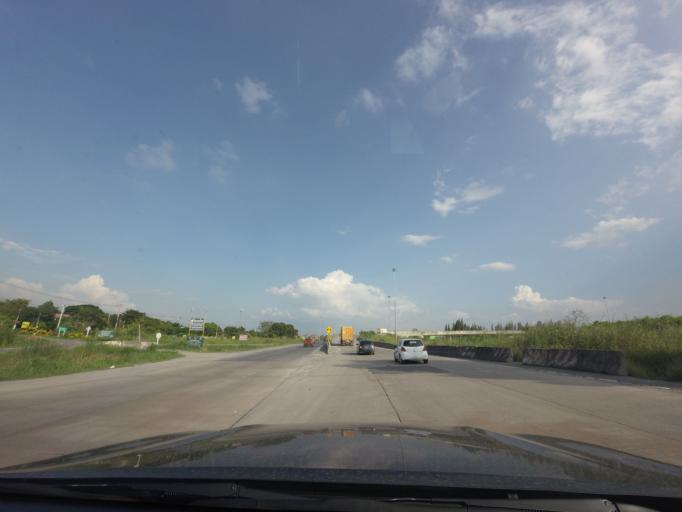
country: TH
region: Sara Buri
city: Saraburi
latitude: 14.5657
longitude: 100.9050
